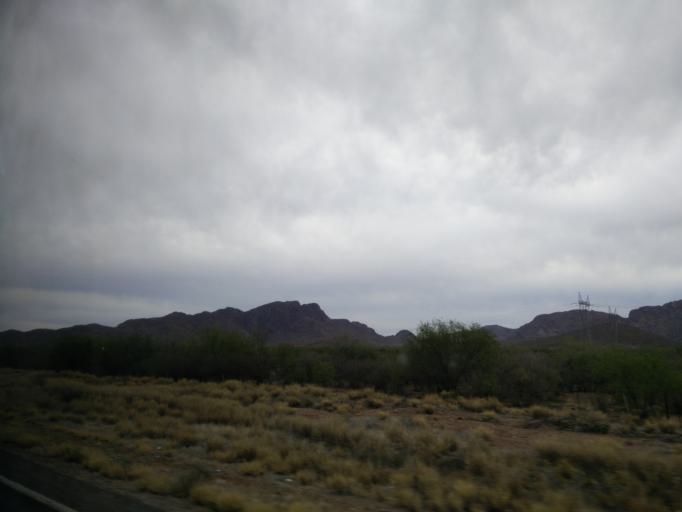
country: MX
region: Sonora
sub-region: Hermosillo
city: Miguel Aleman (La Doce)
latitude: 28.5762
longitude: -111.0300
